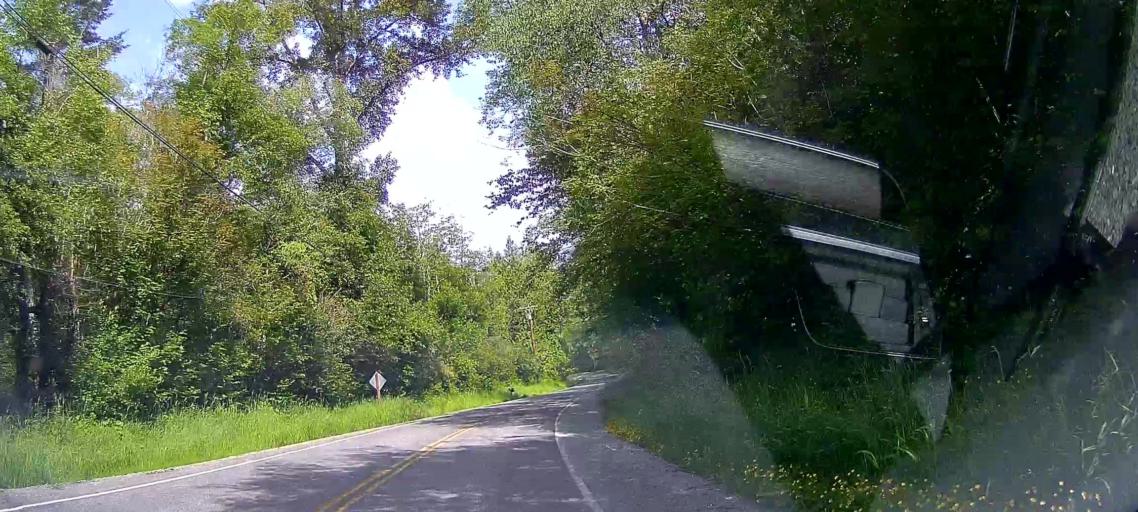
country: US
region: Washington
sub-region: Skagit County
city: Burlington
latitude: 48.5736
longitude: -122.3817
